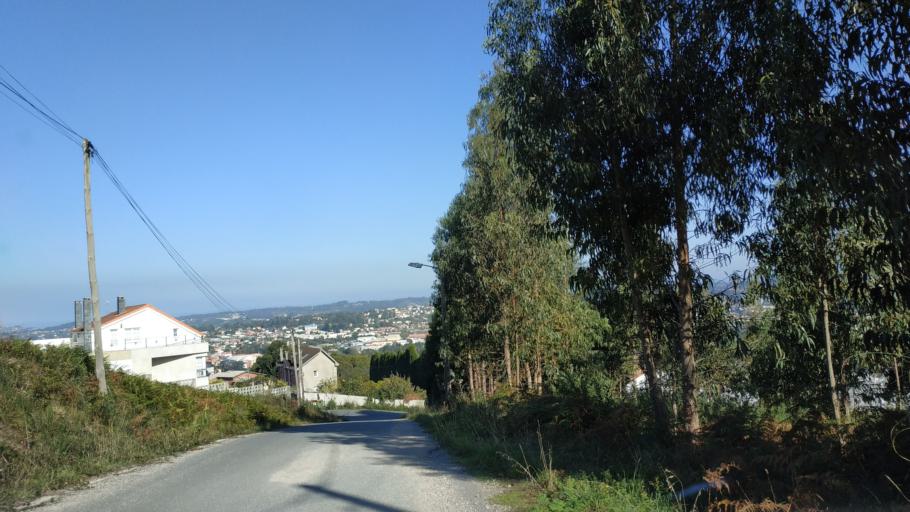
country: ES
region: Galicia
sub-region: Provincia da Coruna
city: Culleredo
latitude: 43.3217
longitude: -8.3875
